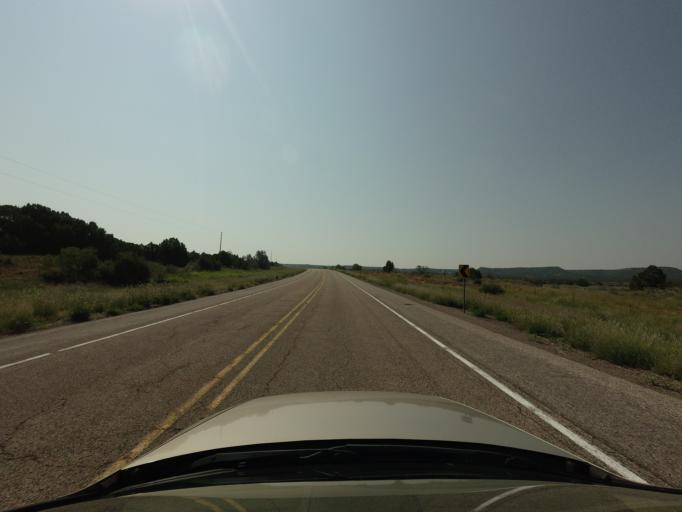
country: US
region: New Mexico
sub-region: Quay County
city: Tucumcari
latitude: 34.8397
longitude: -103.7600
